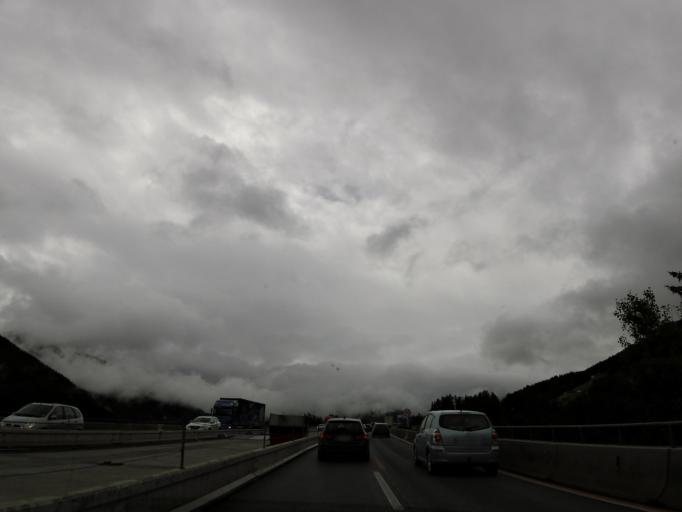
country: AT
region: Tyrol
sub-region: Politischer Bezirk Innsbruck Land
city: Steinach am Brenner
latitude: 47.0695
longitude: 11.4806
